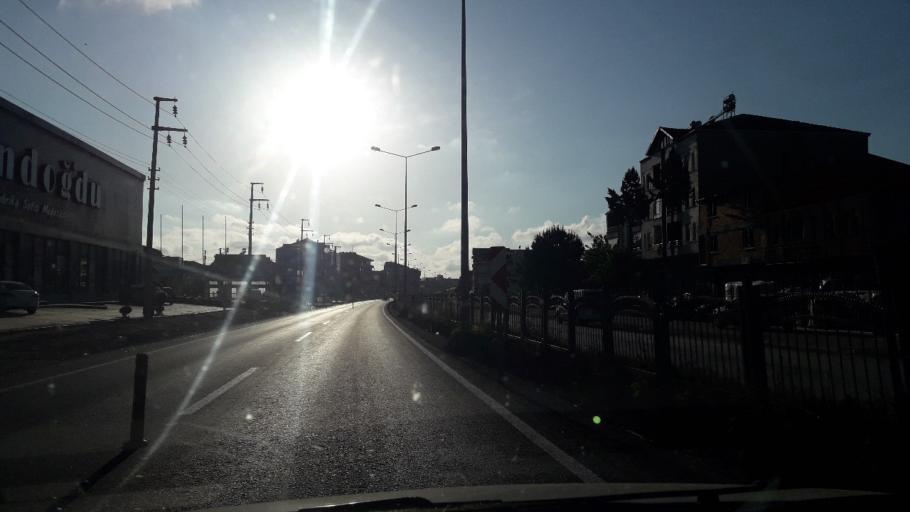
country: TR
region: Samsun
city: Bafra
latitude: 41.5581
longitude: 35.9015
